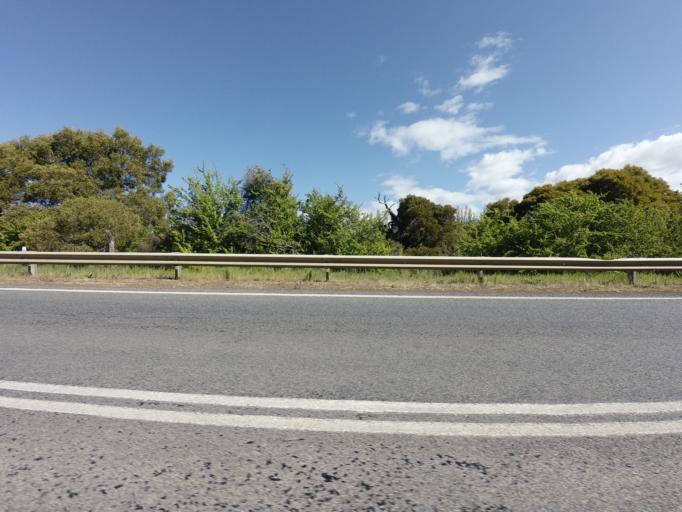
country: AU
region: Tasmania
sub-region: Derwent Valley
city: New Norfolk
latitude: -42.7364
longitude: 146.9559
